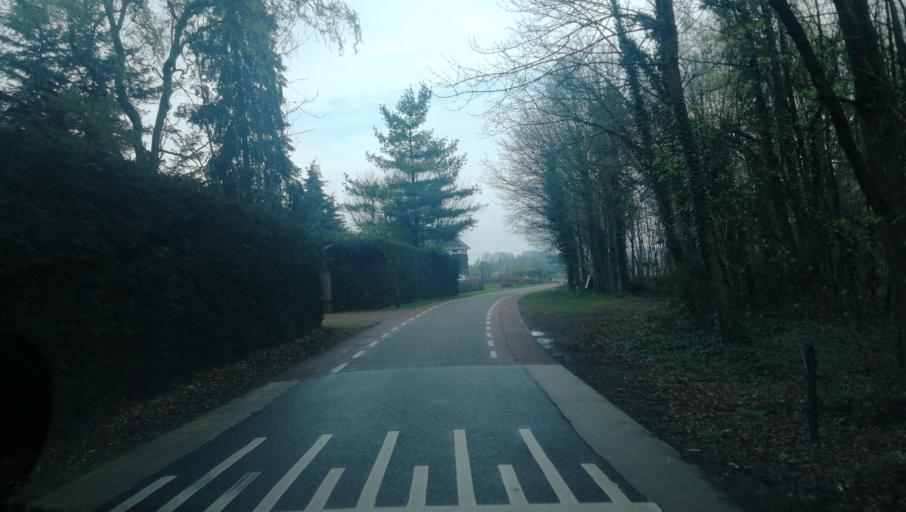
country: NL
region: Limburg
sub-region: Gemeente Beesel
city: Beesel
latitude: 51.3115
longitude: 5.9957
